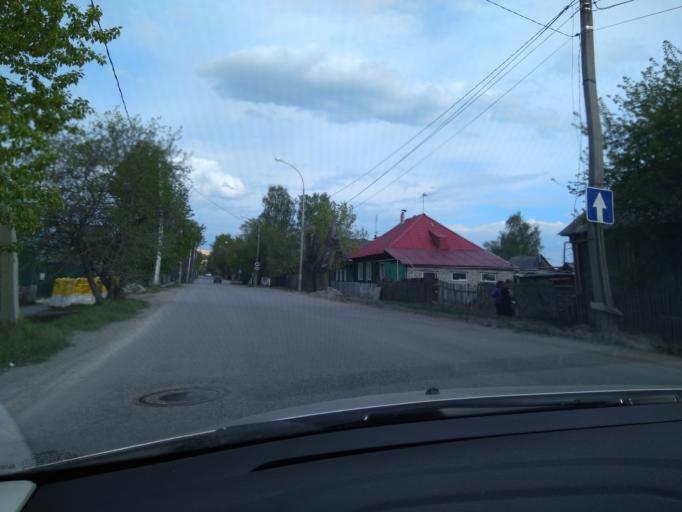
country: RU
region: Sverdlovsk
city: Yekaterinburg
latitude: 56.8822
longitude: 60.5514
